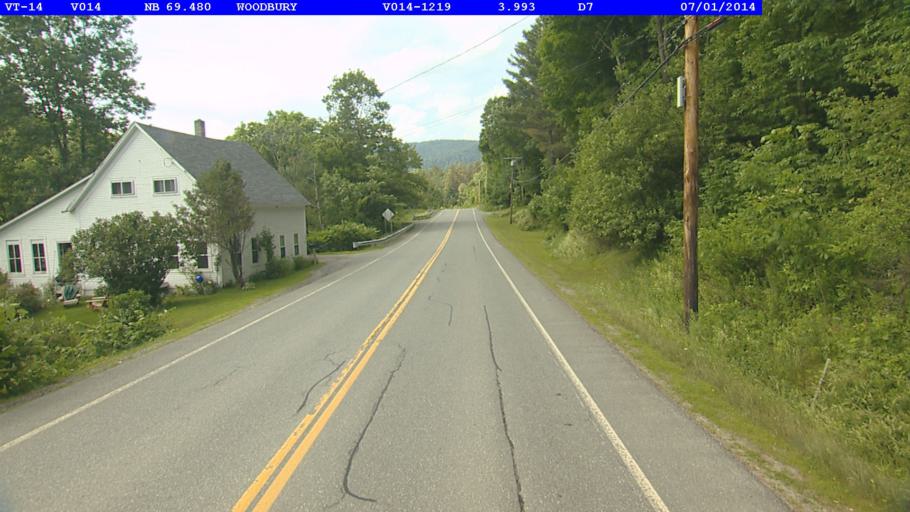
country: US
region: Vermont
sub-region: Caledonia County
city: Hardwick
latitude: 44.4455
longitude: -72.4160
